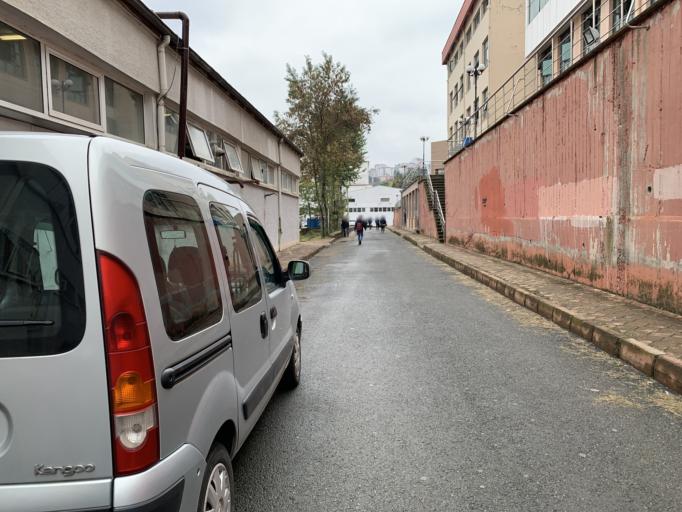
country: TR
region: Trabzon
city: Trabzon
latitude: 40.9937
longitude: 39.7737
